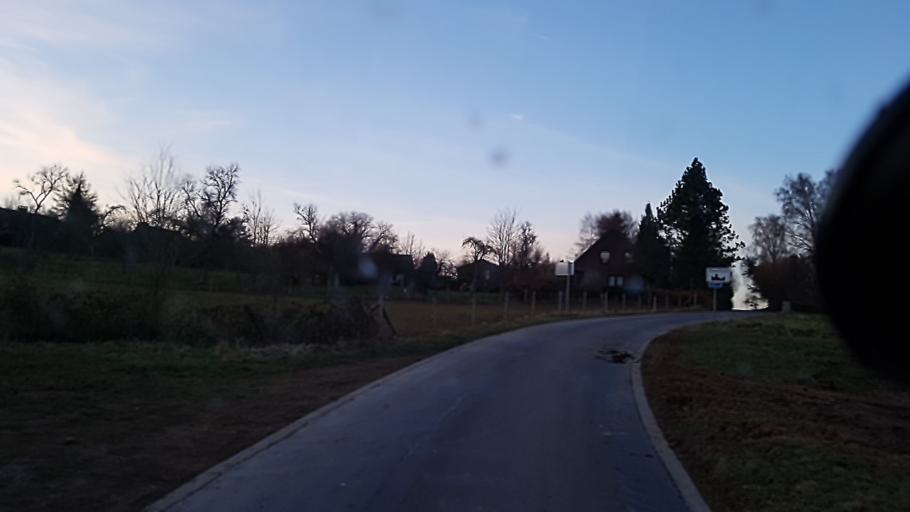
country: BE
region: Wallonia
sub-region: Province du Luxembourg
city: Daverdisse
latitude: 50.0188
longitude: 5.1202
